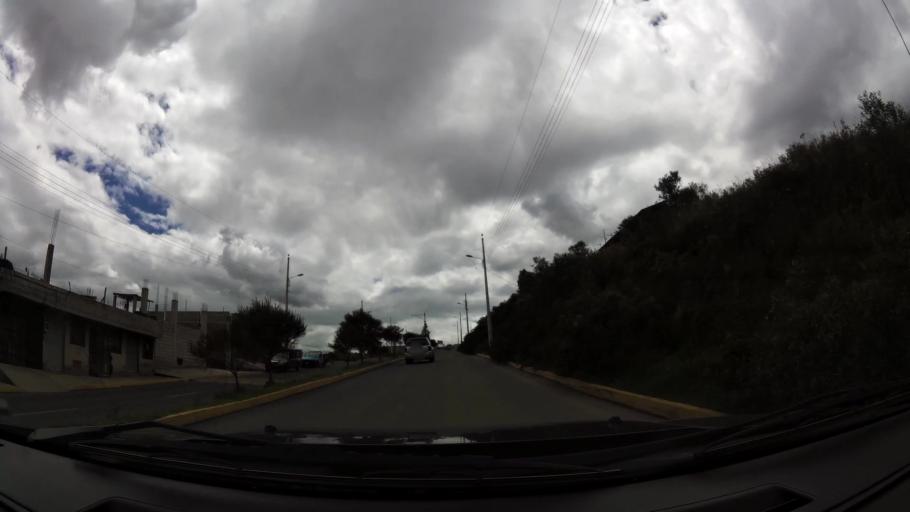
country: EC
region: Pichincha
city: Sangolqui
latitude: -0.3290
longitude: -78.5257
